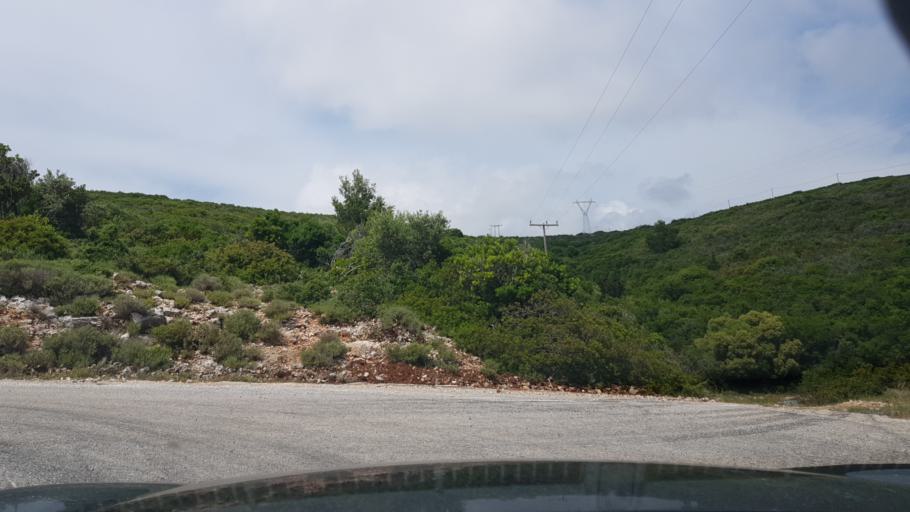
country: GR
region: Ionian Islands
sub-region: Lefkada
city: Nidri
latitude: 38.5947
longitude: 20.5561
